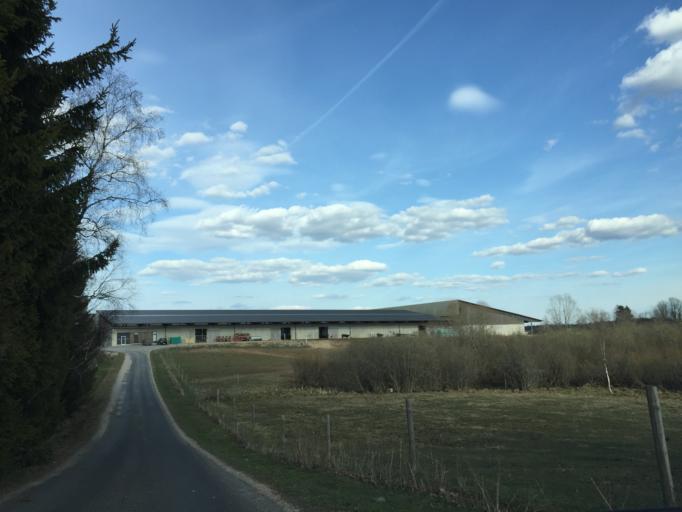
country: EE
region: Tartu
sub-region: Noo vald
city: Noo
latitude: 58.1312
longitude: 26.5885
